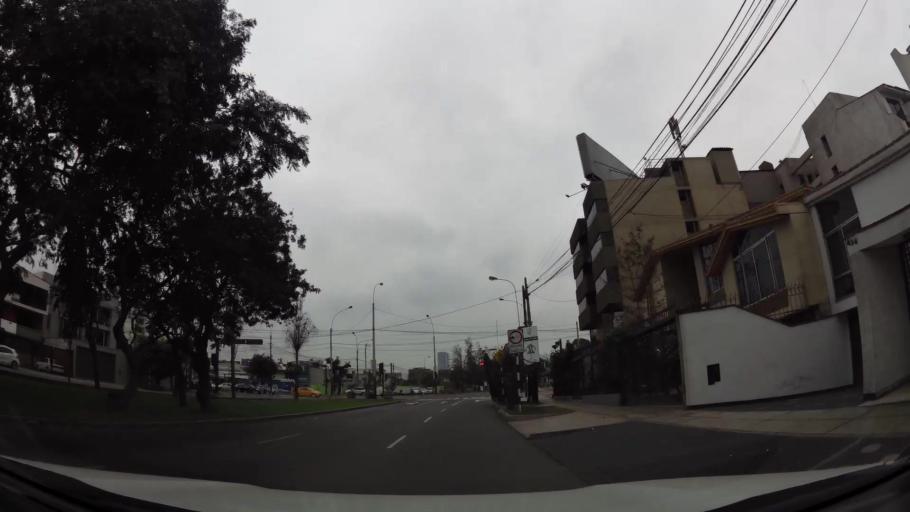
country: PE
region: Lima
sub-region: Lima
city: San Luis
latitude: -12.0921
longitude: -77.0144
